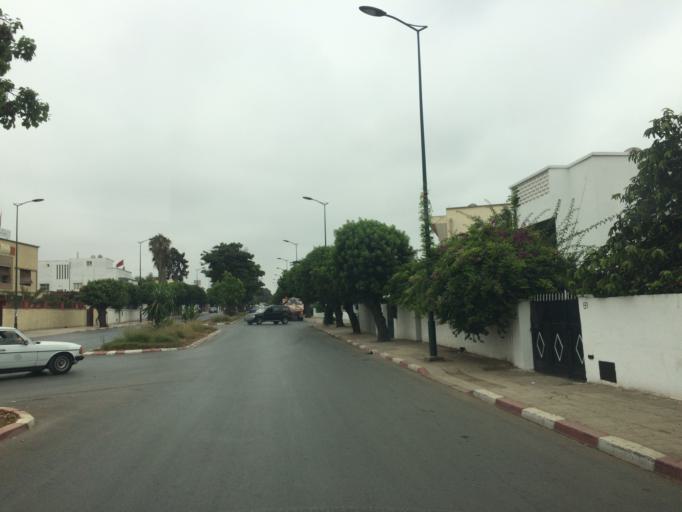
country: MA
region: Rabat-Sale-Zemmour-Zaer
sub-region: Rabat
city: Rabat
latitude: 33.9920
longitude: -6.8183
